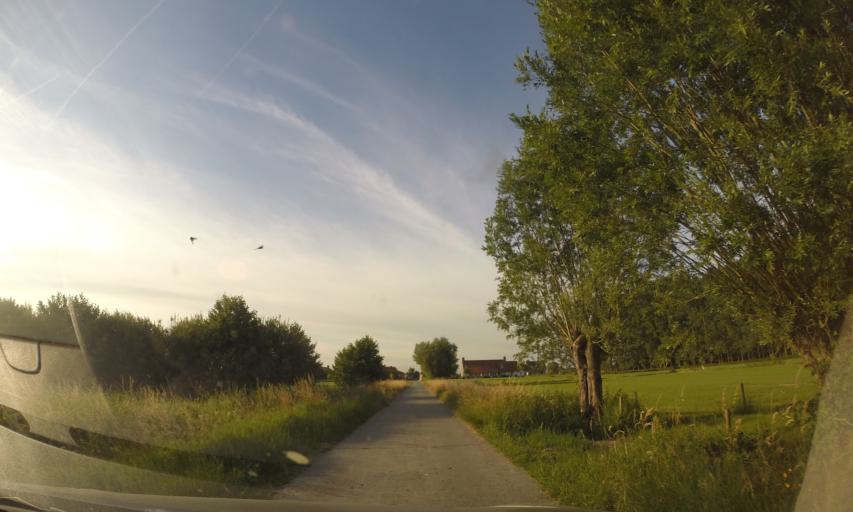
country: BE
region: Flanders
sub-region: Provincie Oost-Vlaanderen
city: Aalter
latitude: 51.1164
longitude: 3.4870
